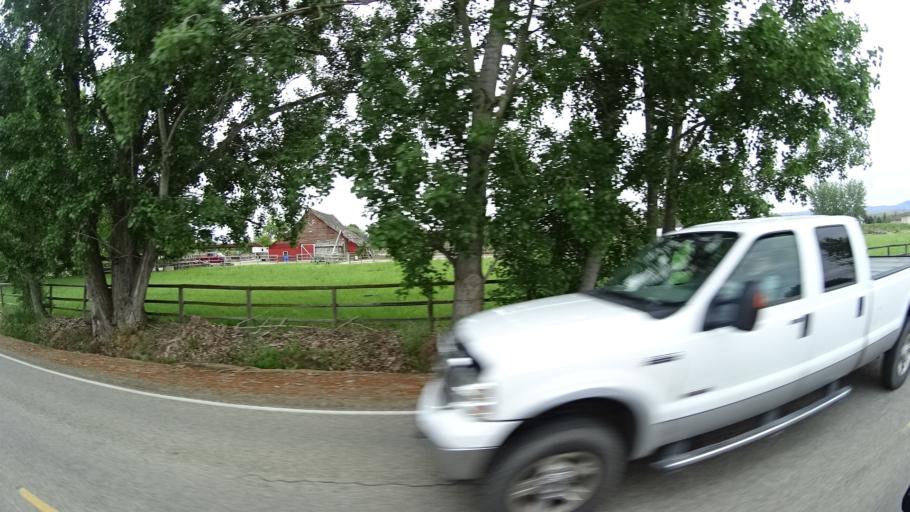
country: US
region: Idaho
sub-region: Ada County
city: Eagle
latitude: 43.7208
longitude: -116.3837
